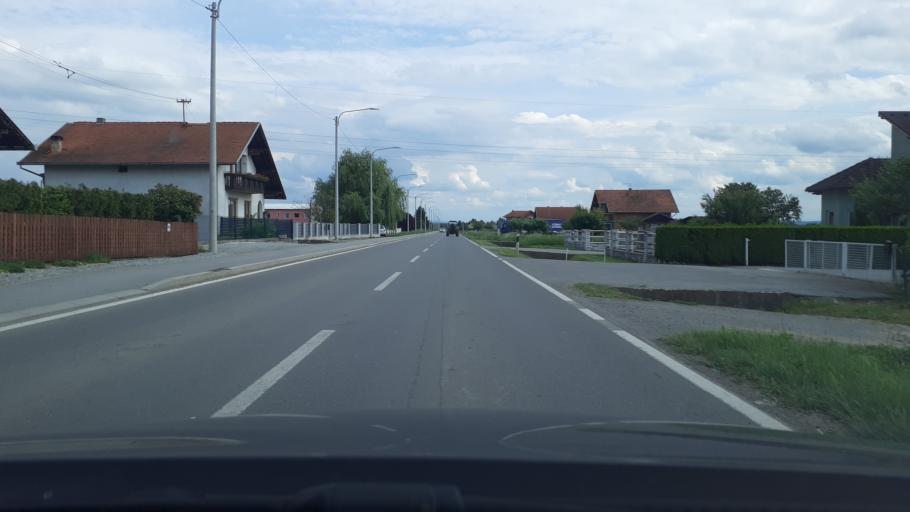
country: HR
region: Brodsko-Posavska
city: Sibinj
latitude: 45.1829
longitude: 17.9246
